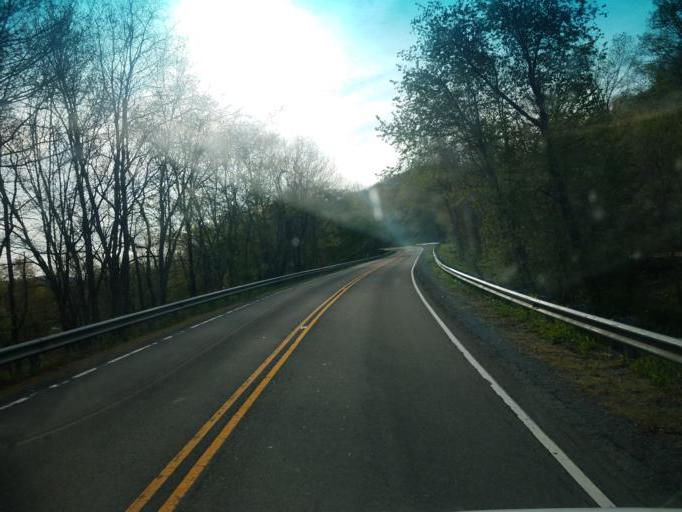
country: US
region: Virginia
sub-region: Smyth County
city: Atkins
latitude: 36.8178
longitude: -81.4391
